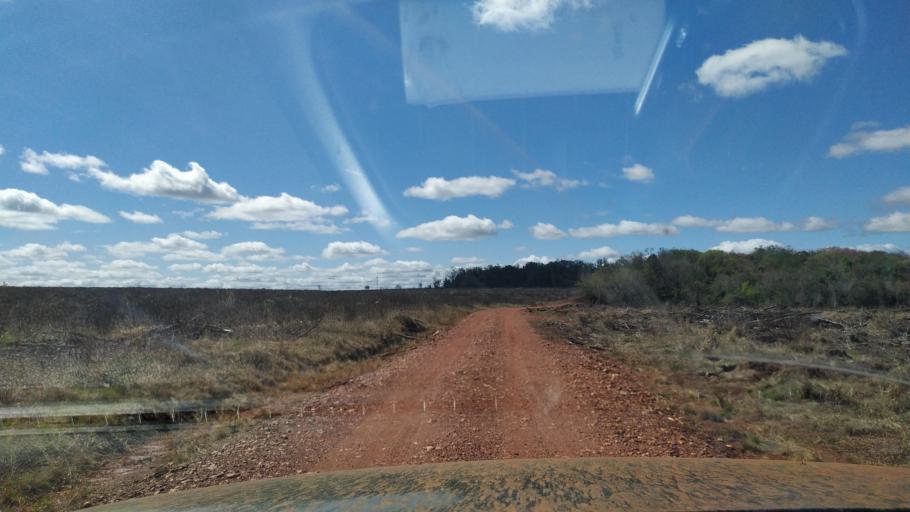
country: AR
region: Corrientes
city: Gobernador Ingeniero Valentin Virasoro
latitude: -28.2915
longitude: -56.0518
